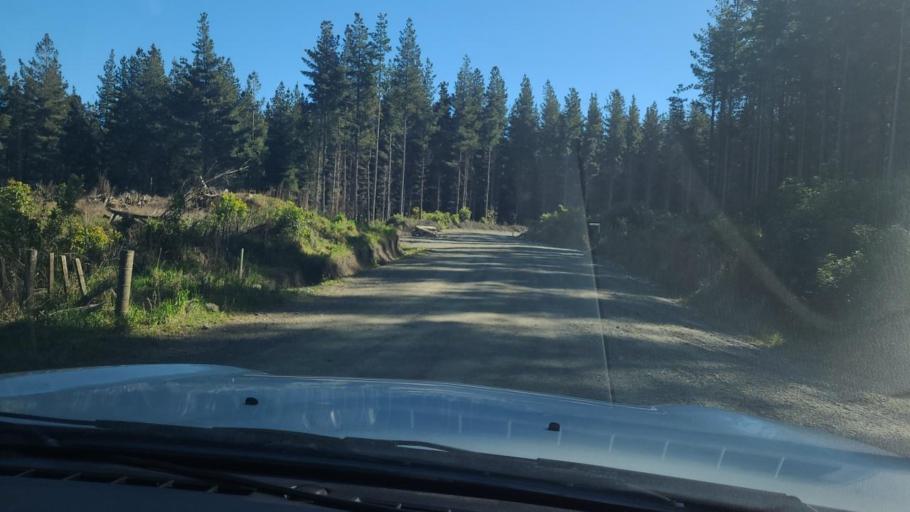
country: NZ
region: Hawke's Bay
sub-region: Napier City
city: Taradale
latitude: -39.4148
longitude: 176.4618
